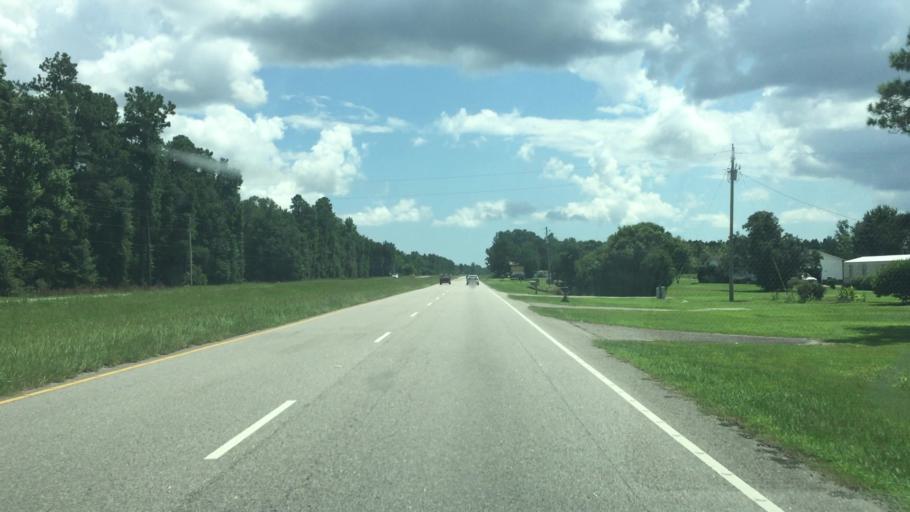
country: US
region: South Carolina
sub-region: Horry County
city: Loris
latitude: 33.9813
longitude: -78.7450
